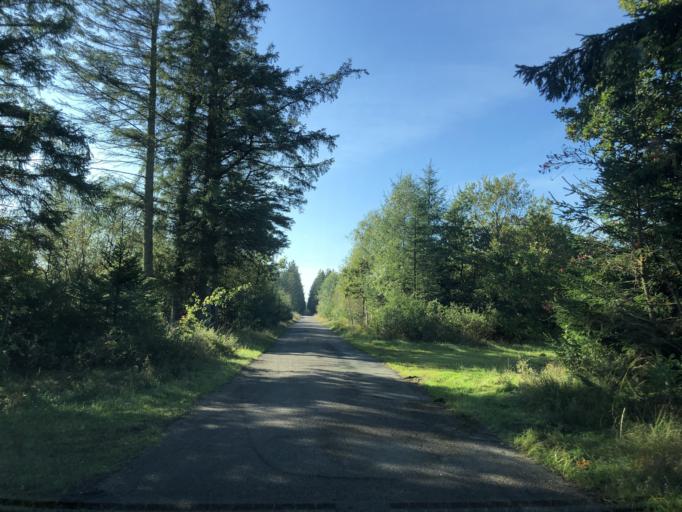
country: DK
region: Central Jutland
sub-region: Holstebro Kommune
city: Holstebro
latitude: 56.3195
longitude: 8.5090
